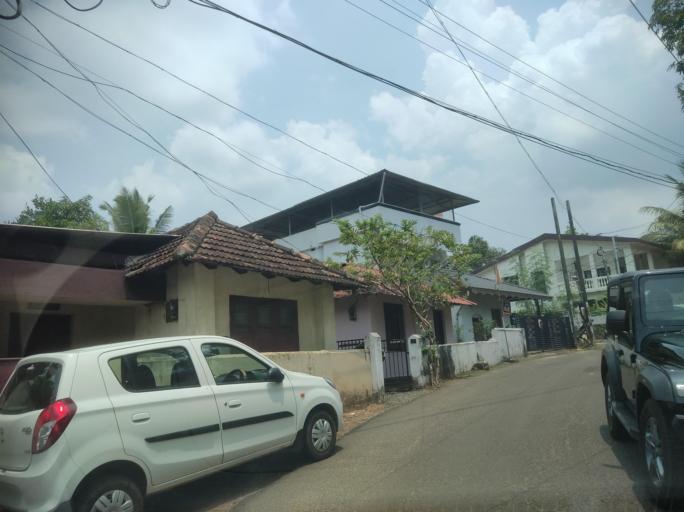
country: IN
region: Kerala
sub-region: Kottayam
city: Kottayam
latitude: 9.5867
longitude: 76.5288
